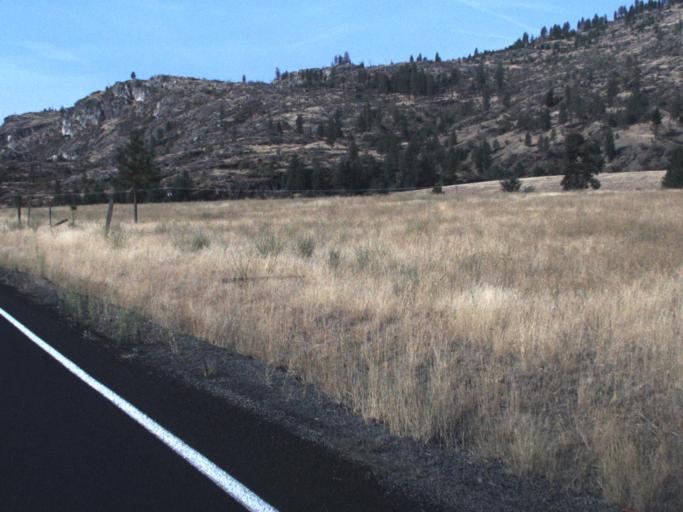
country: US
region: Washington
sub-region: Spokane County
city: Deer Park
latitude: 47.8672
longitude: -117.7077
